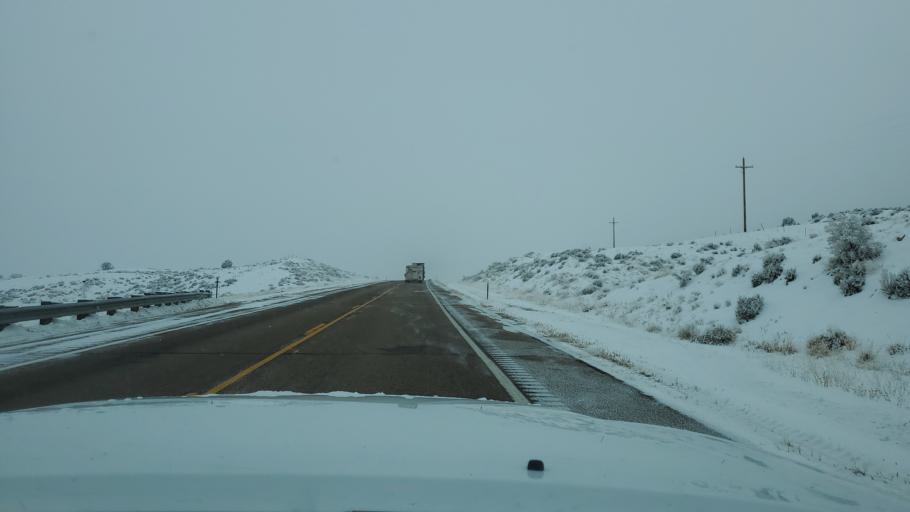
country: US
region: Colorado
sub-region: Rio Blanco County
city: Rangely
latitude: 40.2427
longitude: -108.9557
